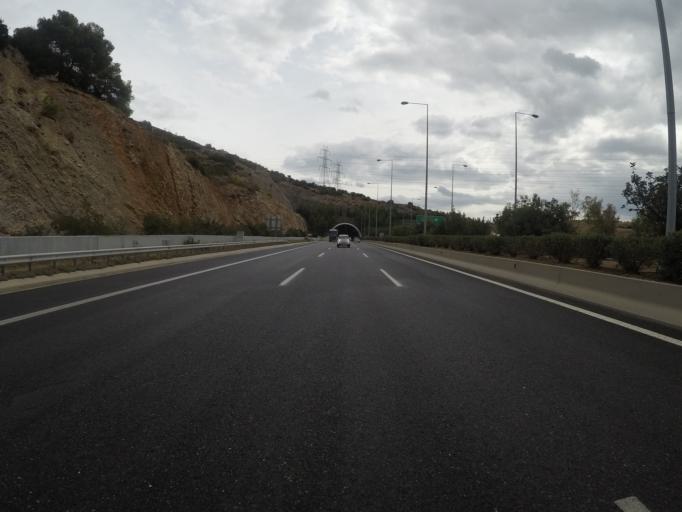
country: GR
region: Attica
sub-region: Nomarchia Dytikis Attikis
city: Fyli
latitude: 38.0833
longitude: 23.6671
